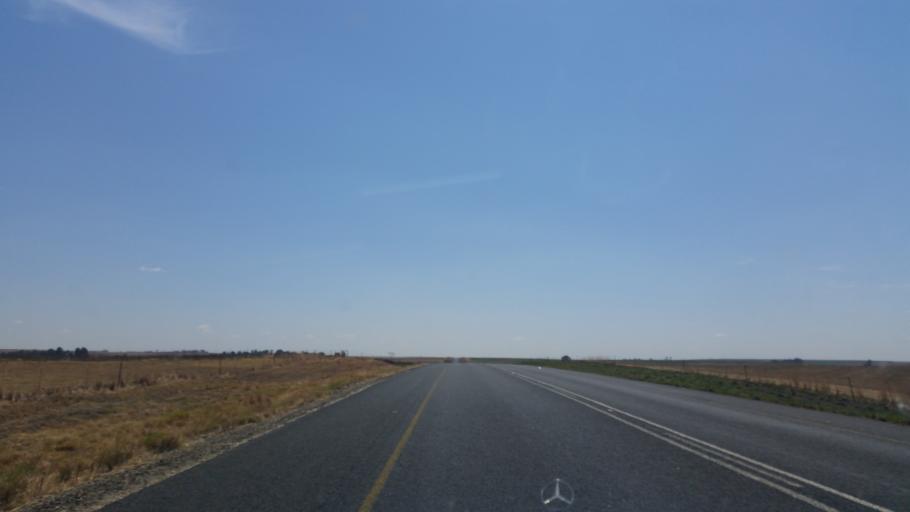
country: ZA
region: Orange Free State
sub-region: Thabo Mofutsanyana District Municipality
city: Phuthaditjhaba
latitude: -28.1873
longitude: 28.6861
